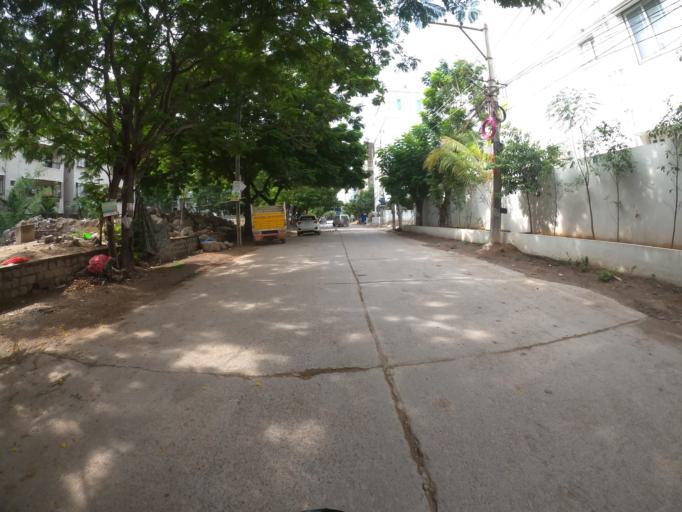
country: IN
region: Telangana
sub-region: Hyderabad
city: Hyderabad
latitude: 17.4084
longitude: 78.3846
